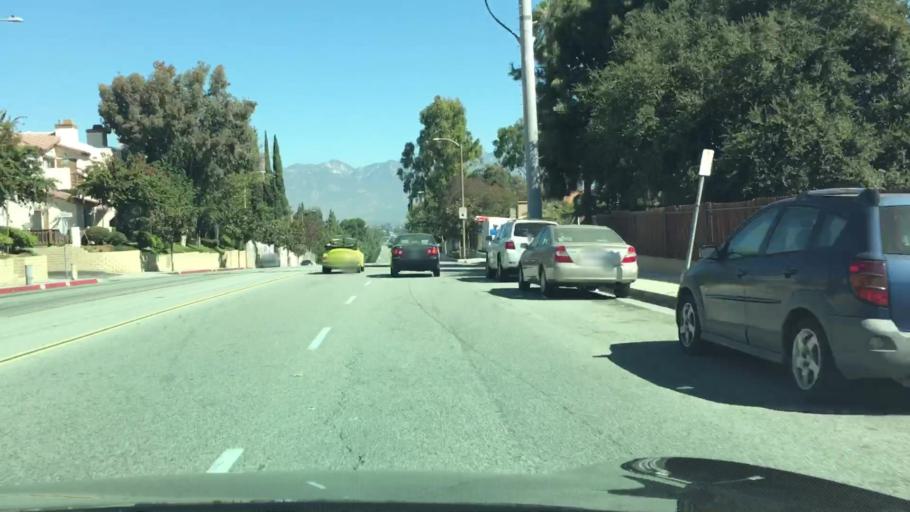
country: US
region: California
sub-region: Los Angeles County
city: South San Gabriel
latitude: 34.0418
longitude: -118.0818
